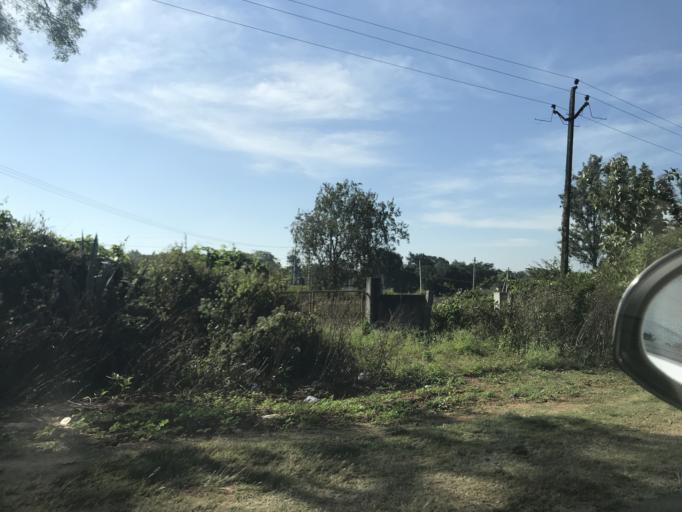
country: IN
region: Karnataka
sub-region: Mysore
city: Mysore
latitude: 12.2175
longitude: 76.5696
